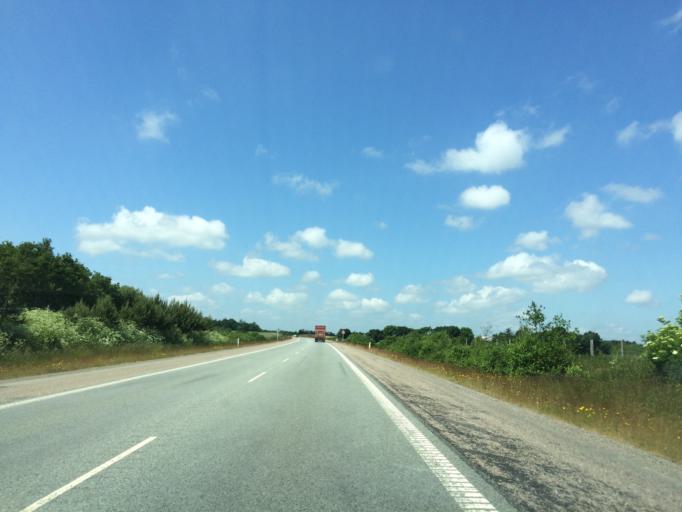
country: DK
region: Central Jutland
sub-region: Herning Kommune
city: Herning
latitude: 56.1835
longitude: 8.9658
